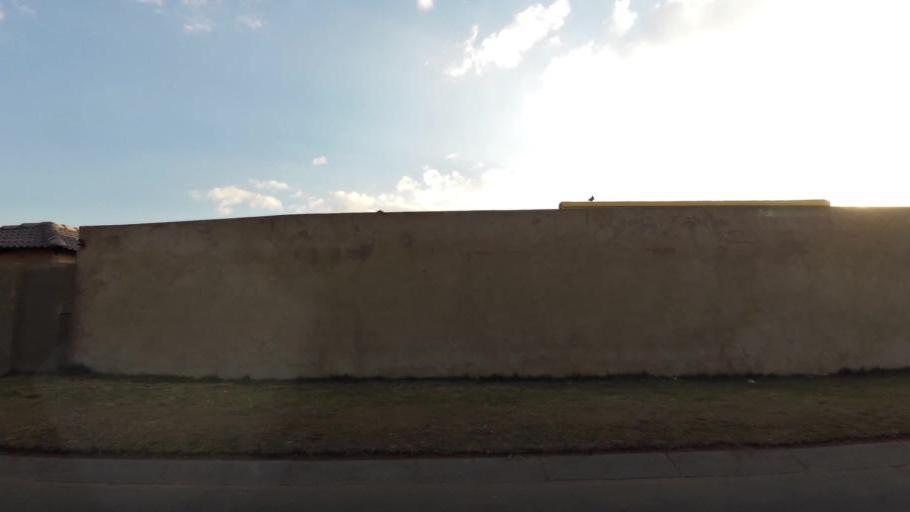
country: ZA
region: Gauteng
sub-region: City of Johannesburg Metropolitan Municipality
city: Roodepoort
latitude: -26.2101
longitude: 27.8989
